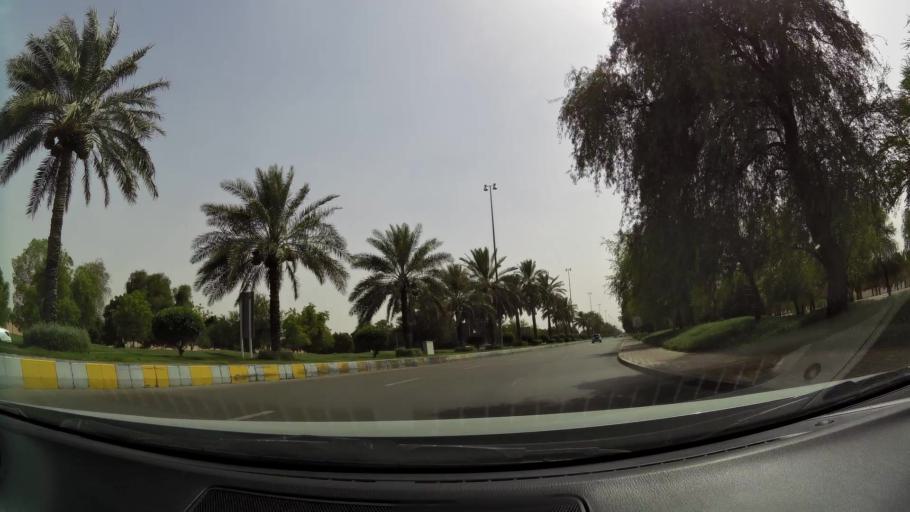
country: AE
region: Abu Dhabi
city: Al Ain
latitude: 24.1938
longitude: 55.6534
